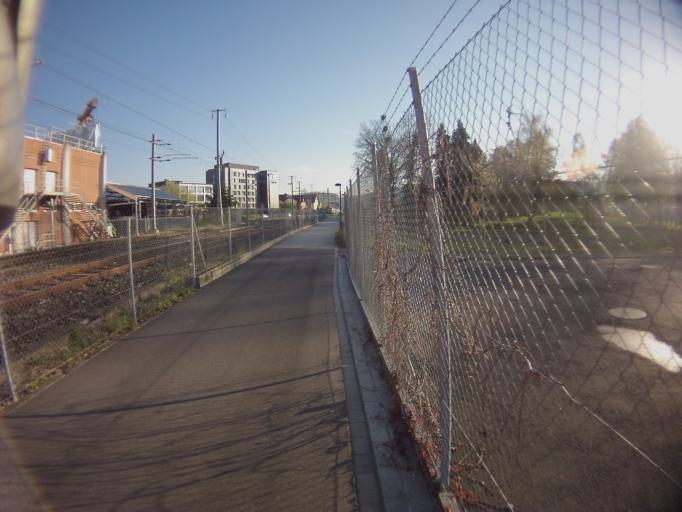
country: CH
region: Zurich
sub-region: Bezirk Affoltern
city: Affoltern / Oberdorf
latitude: 47.2728
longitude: 8.4431
